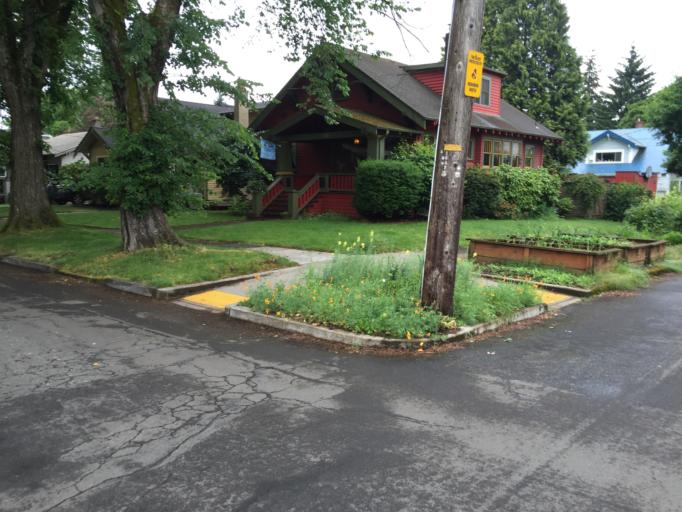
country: US
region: Oregon
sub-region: Multnomah County
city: Portland
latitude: 45.5352
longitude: -122.6109
